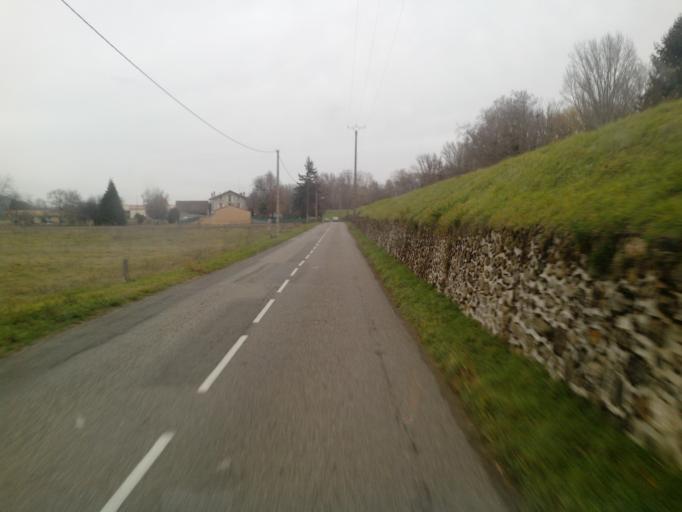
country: FR
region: Midi-Pyrenees
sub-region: Departement de l'Ariege
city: Saint-Jean-du-Falga
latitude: 43.0728
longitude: 1.6188
